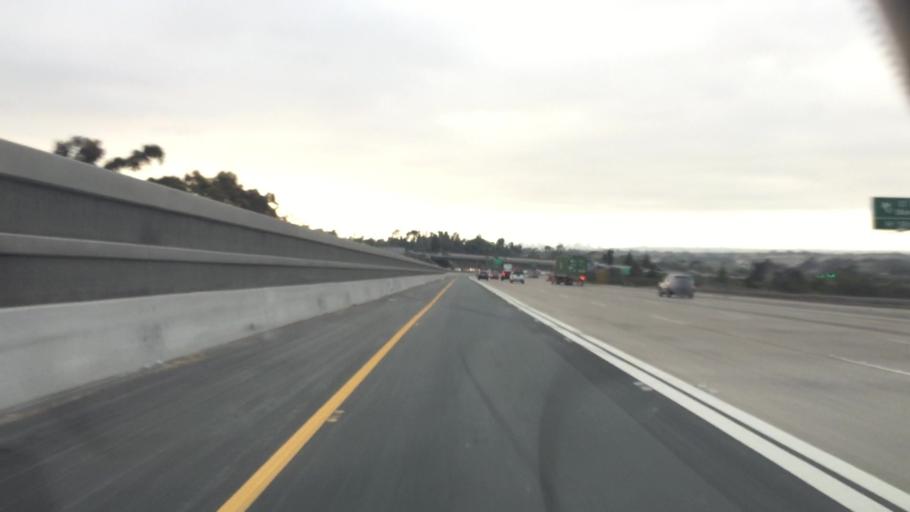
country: US
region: California
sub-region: San Diego County
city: Bonita
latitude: 32.6377
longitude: -117.0511
